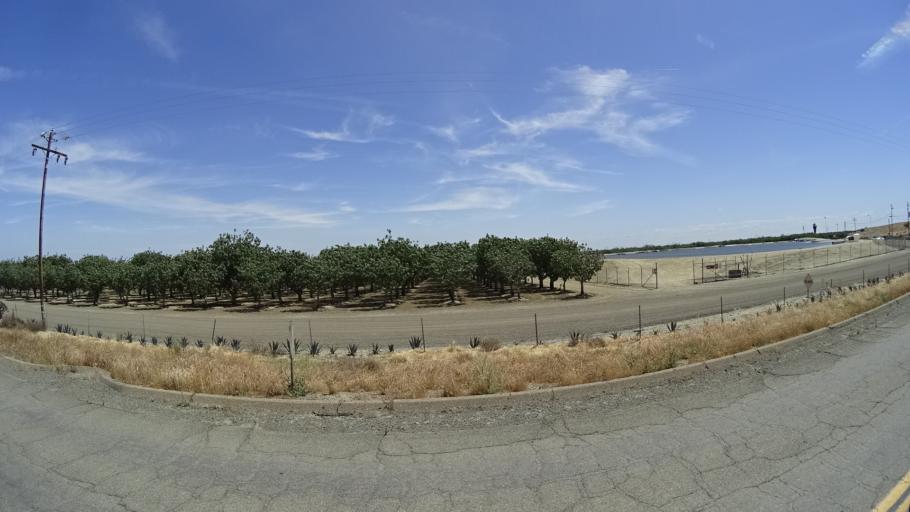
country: US
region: California
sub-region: Kings County
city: Kettleman City
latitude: 35.9083
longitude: -119.9150
